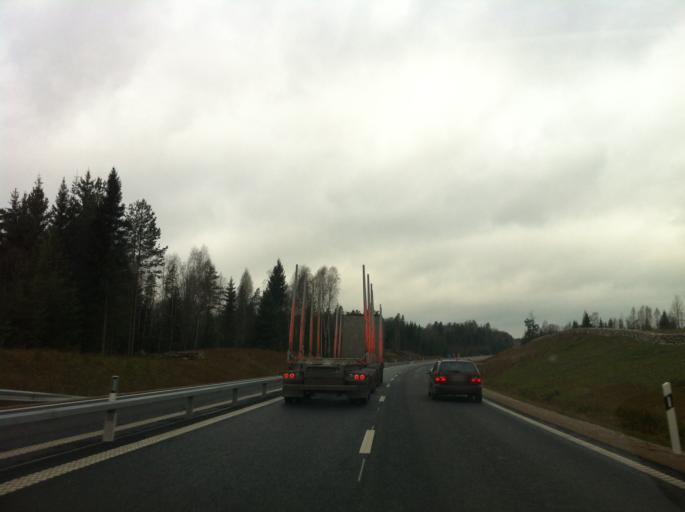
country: SE
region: Joenkoeping
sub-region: Vetlanda Kommun
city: Vetlanda
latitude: 57.4170
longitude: 15.2142
